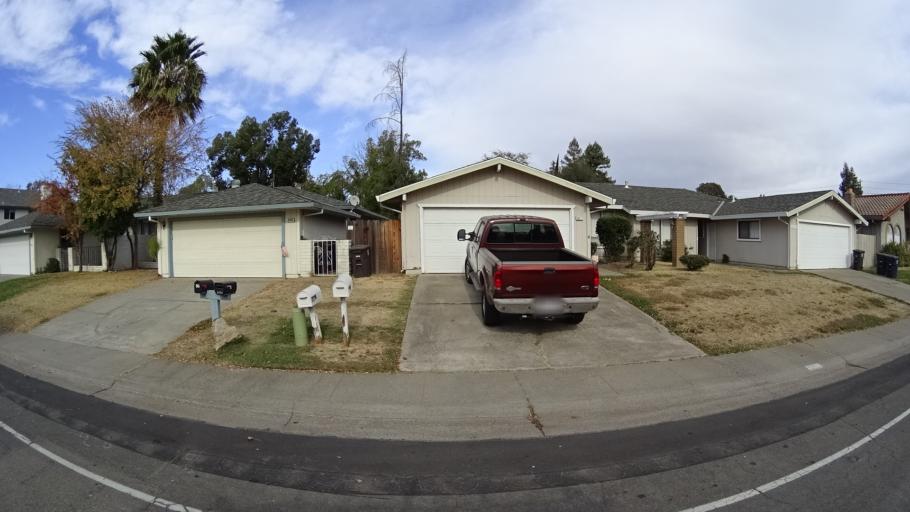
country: US
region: California
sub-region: Sacramento County
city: Fair Oaks
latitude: 38.6684
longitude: -121.2635
